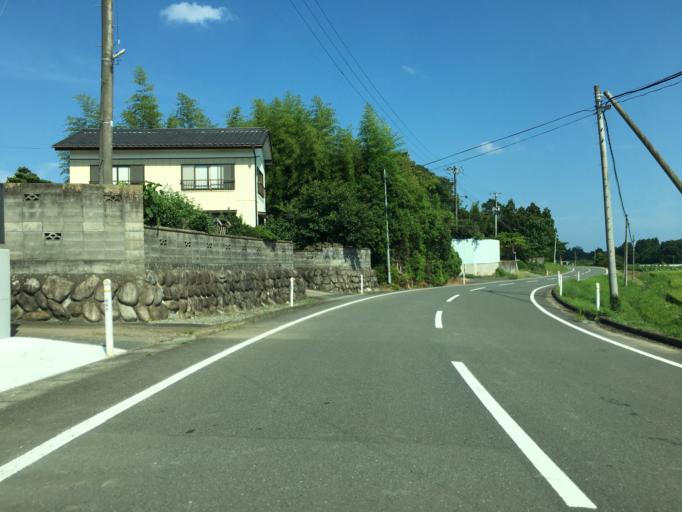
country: JP
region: Miyagi
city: Marumori
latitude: 37.7895
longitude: 140.9346
